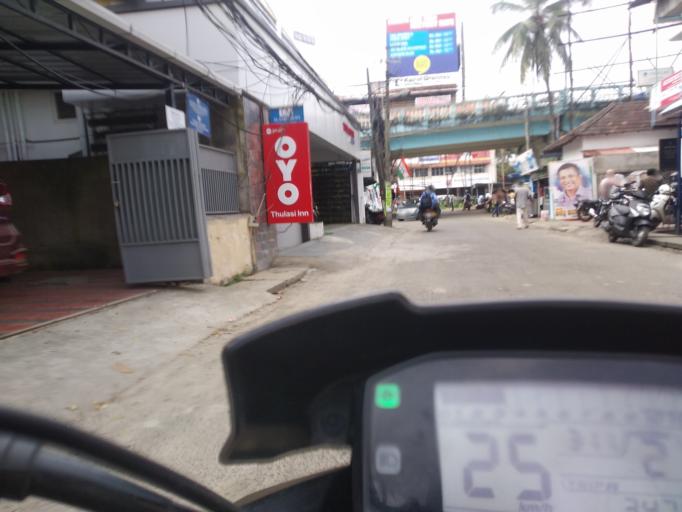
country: IN
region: Kerala
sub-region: Ernakulam
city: Cochin
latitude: 9.9646
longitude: 76.2918
